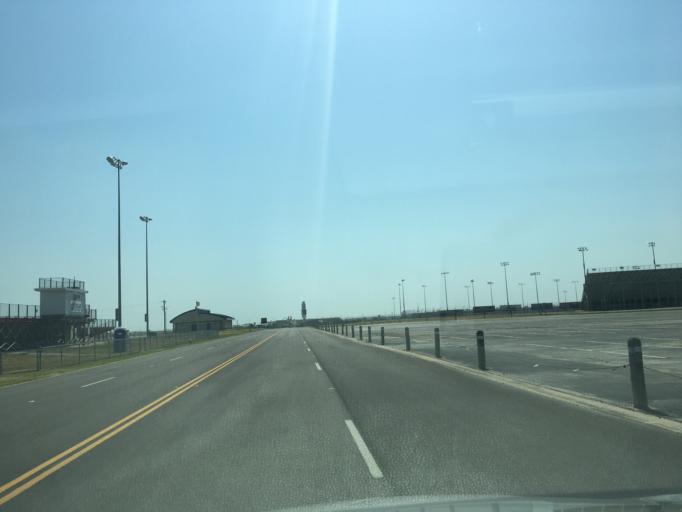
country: US
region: Texas
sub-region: Denton County
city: Justin
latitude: 33.0355
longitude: -97.2768
